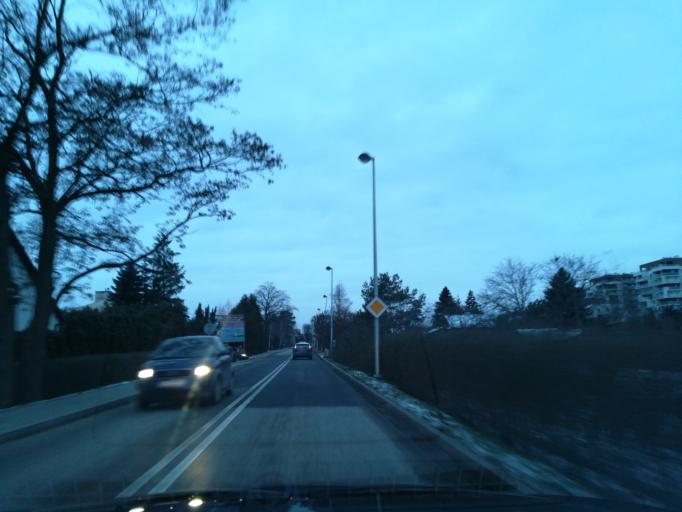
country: PL
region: Subcarpathian Voivodeship
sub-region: Rzeszow
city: Rzeszow
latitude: 50.0144
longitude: 22.0166
